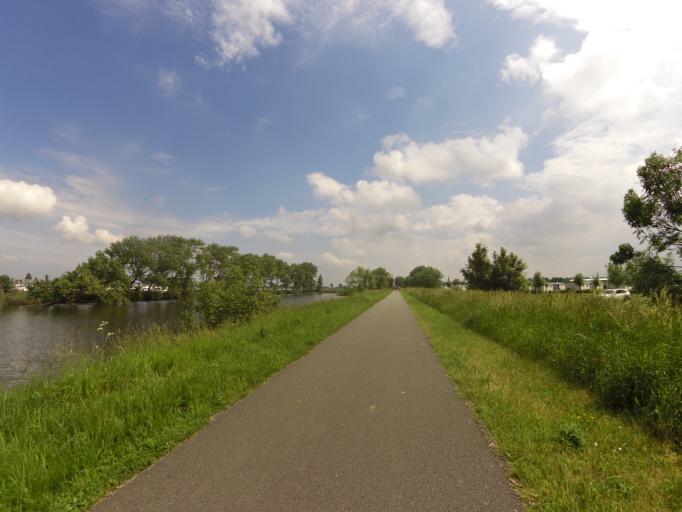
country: BE
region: Flanders
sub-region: Provincie West-Vlaanderen
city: Nieuwpoort
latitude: 51.1329
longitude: 2.7664
